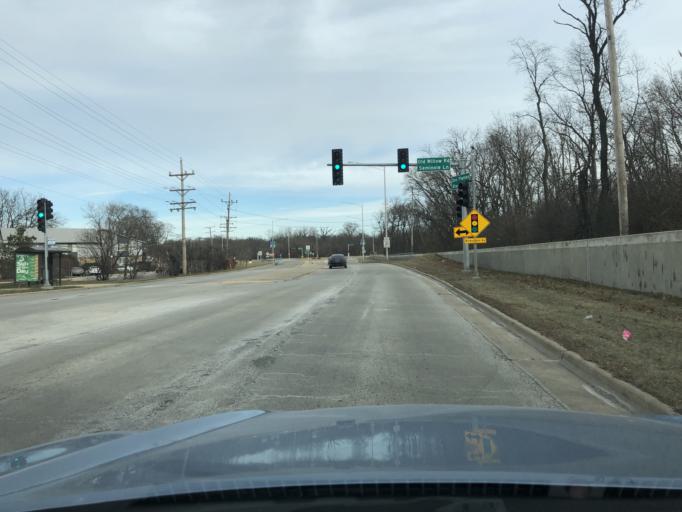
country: US
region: Illinois
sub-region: Cook County
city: Prospect Heights
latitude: 42.1020
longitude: -87.8888
